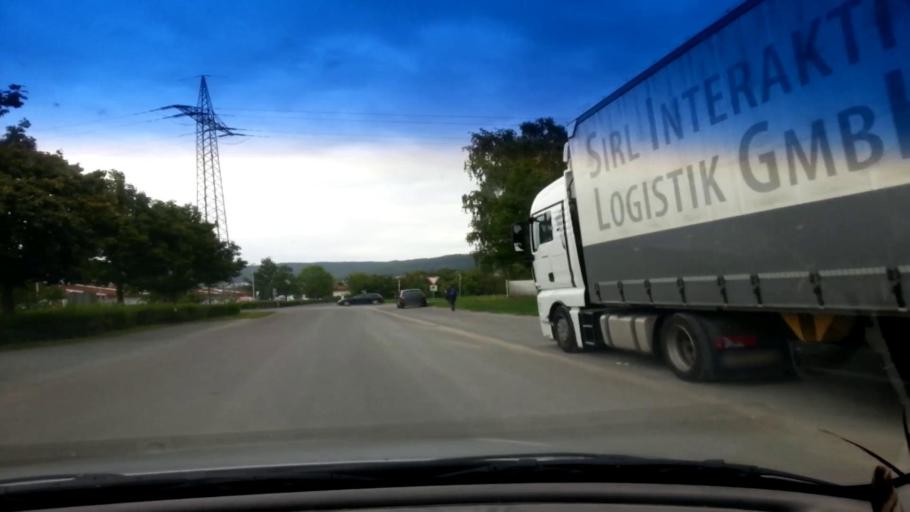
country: DE
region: Bavaria
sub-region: Upper Franconia
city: Hirschaid
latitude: 49.8142
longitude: 11.0040
